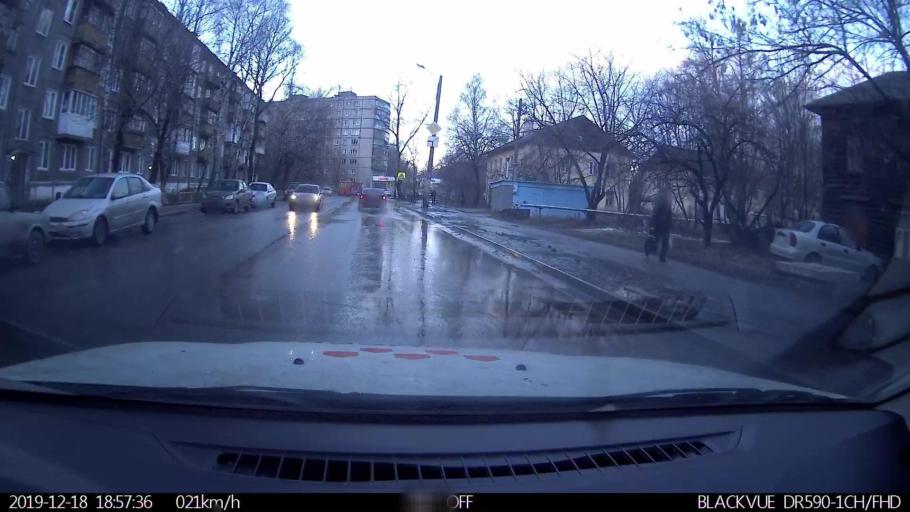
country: RU
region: Nizjnij Novgorod
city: Gorbatovka
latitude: 56.3375
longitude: 43.8412
